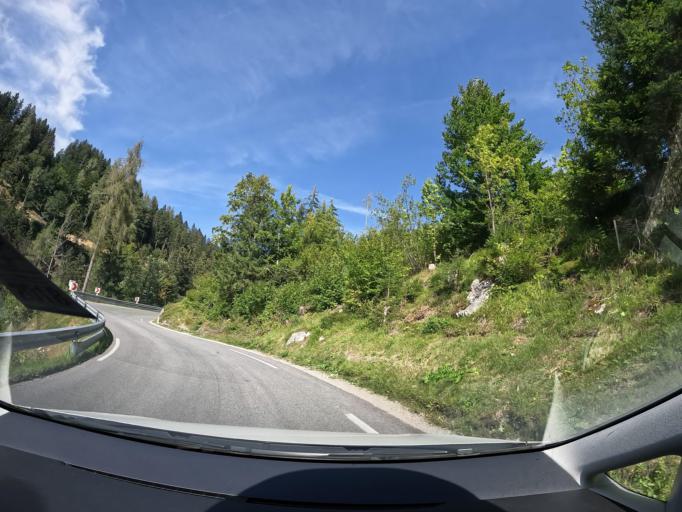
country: AT
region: Carinthia
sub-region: Politischer Bezirk Villach Land
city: Velden am Woerthersee
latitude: 46.5950
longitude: 14.0620
